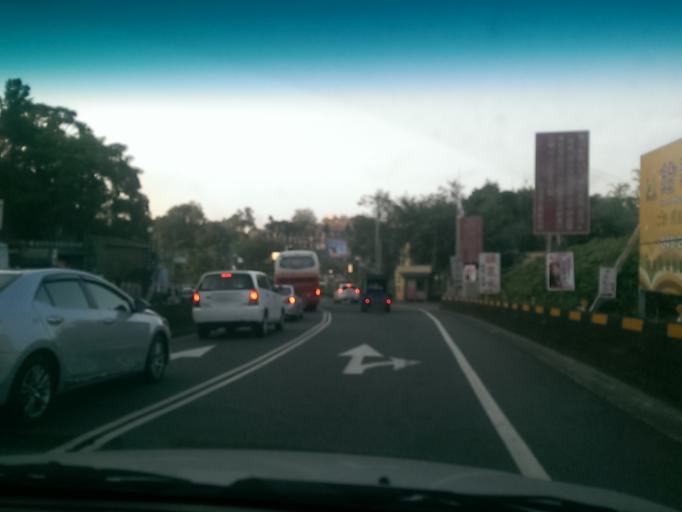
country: TW
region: Taiwan
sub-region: Nantou
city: Puli
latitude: 23.9651
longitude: 120.9467
